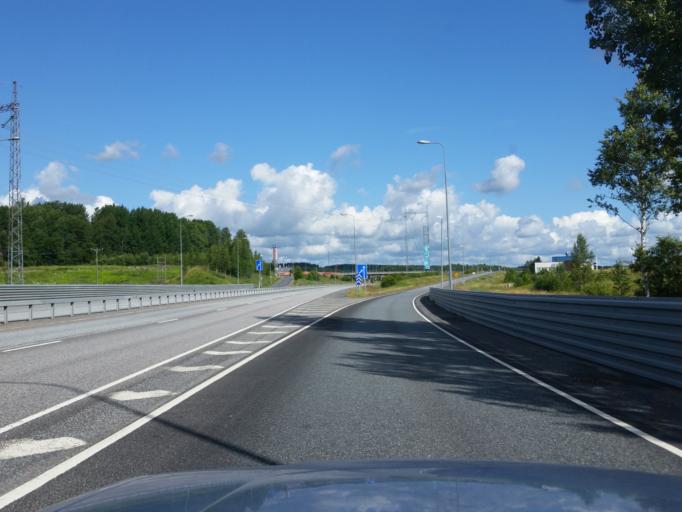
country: FI
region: Uusimaa
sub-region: Helsinki
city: Vihti
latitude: 60.3277
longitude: 24.3353
